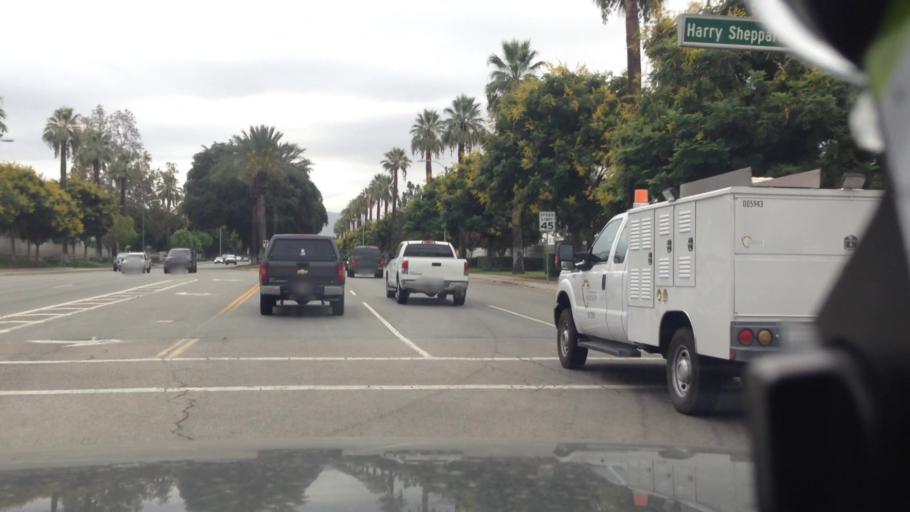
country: US
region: California
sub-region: San Bernardino County
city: San Bernardino
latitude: 34.0981
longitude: -117.2597
